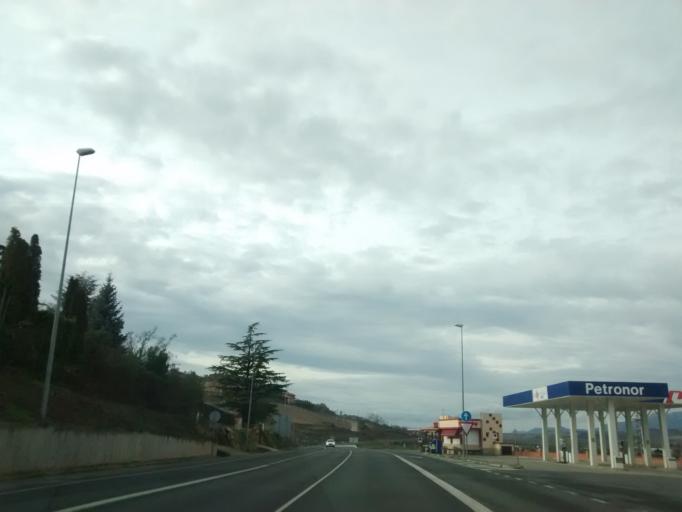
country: ES
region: La Rioja
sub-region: Provincia de La Rioja
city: Cenicero
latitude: 42.4830
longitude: -2.6520
